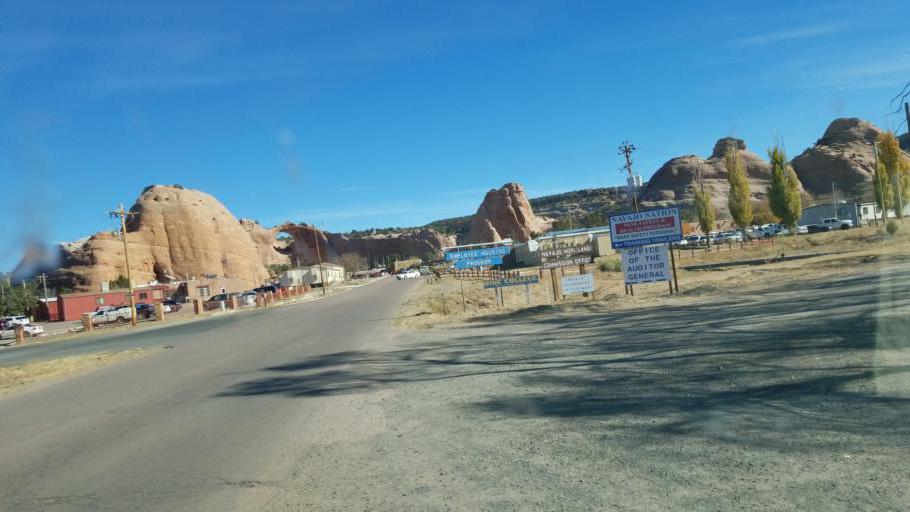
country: US
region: Arizona
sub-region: Apache County
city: Window Rock
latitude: 35.6775
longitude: -109.0519
